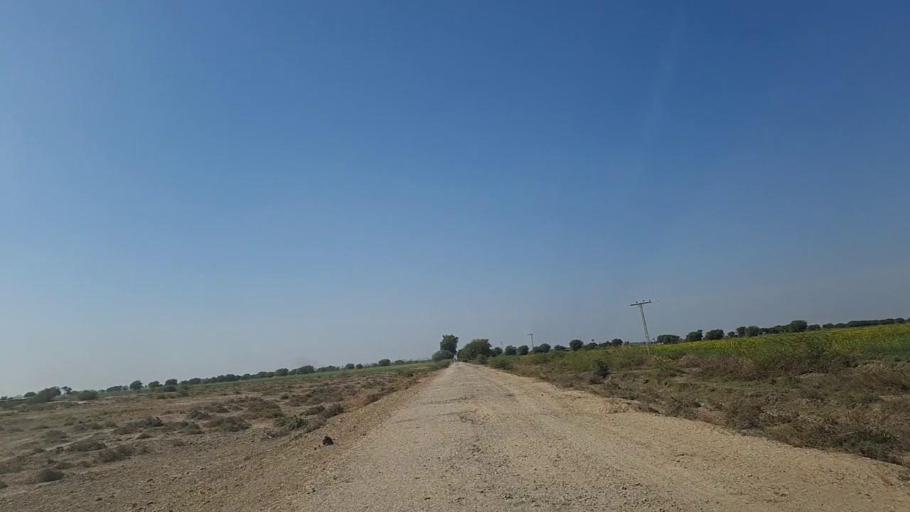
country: PK
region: Sindh
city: Naukot
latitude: 25.0379
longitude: 69.3867
